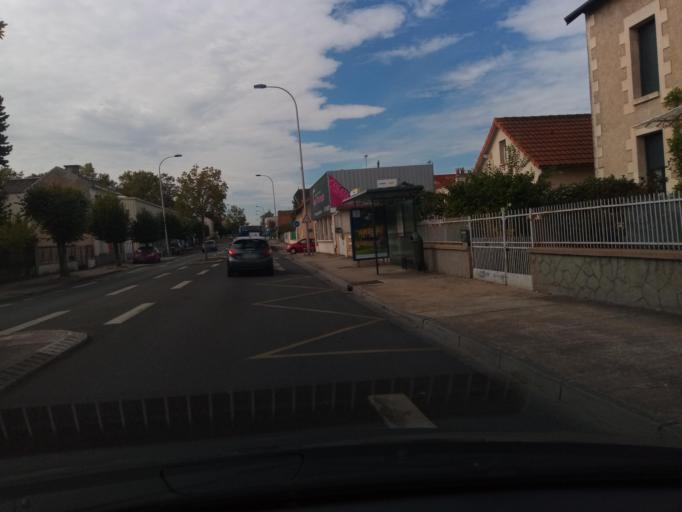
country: FR
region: Poitou-Charentes
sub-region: Departement de la Vienne
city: Biard
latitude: 46.5614
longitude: 0.3148
